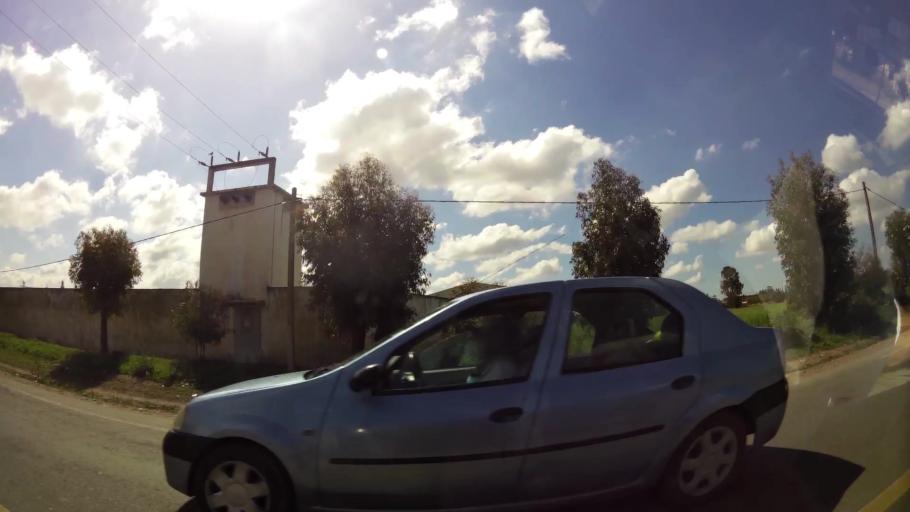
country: MA
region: Grand Casablanca
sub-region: Mediouna
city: Mediouna
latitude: 33.4366
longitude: -7.5208
